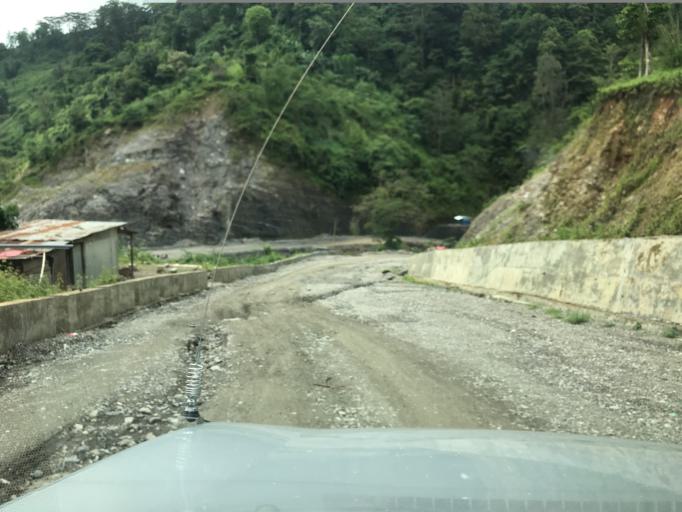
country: TL
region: Aileu
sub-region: Aileu Villa
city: Aileu
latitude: -8.6472
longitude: 125.5248
